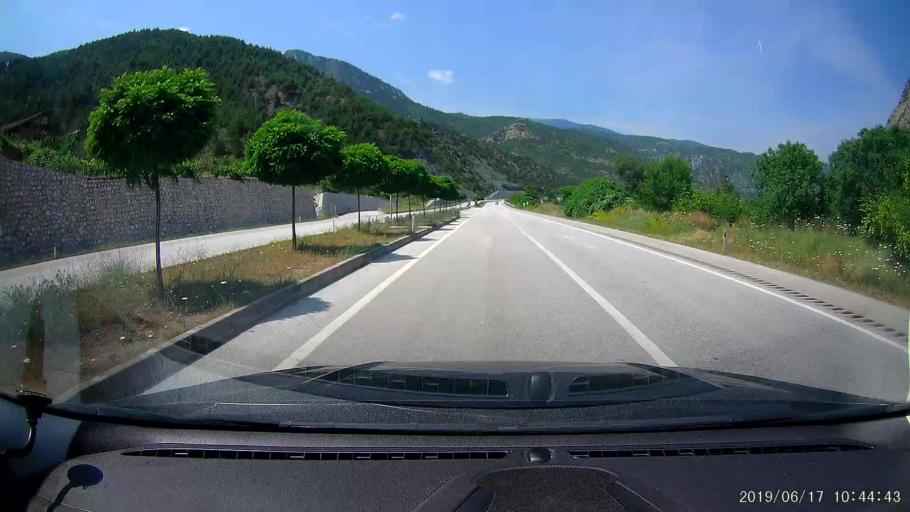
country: TR
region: Corum
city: Hacihamza
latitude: 41.0686
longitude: 34.5055
